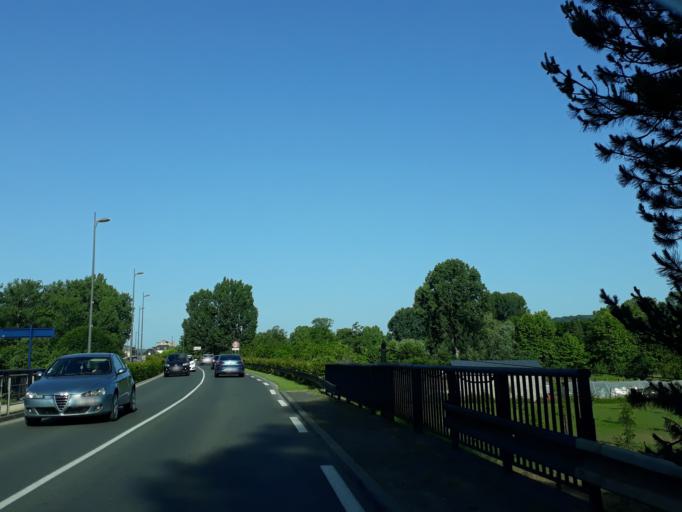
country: FR
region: Aquitaine
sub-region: Departement de la Dordogne
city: Terrasson-Lavilledieu
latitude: 45.1300
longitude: 1.3103
